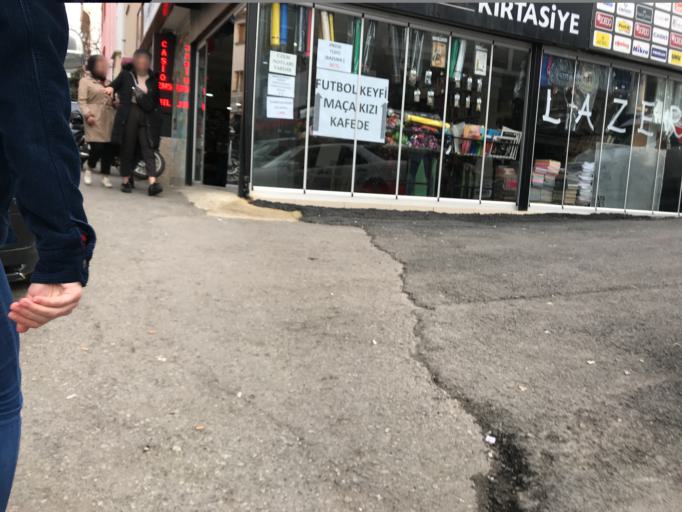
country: TR
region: Trabzon
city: Trabzon
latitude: 40.9913
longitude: 39.7770
